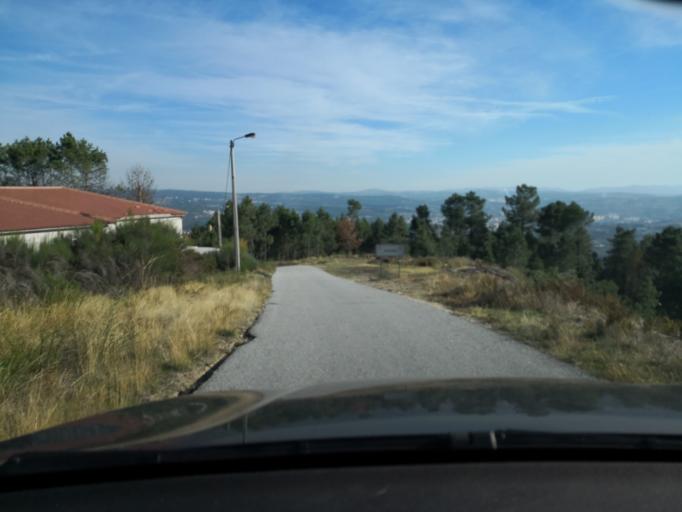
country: PT
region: Vila Real
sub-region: Vila Real
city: Vila Real
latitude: 41.3406
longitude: -7.7505
